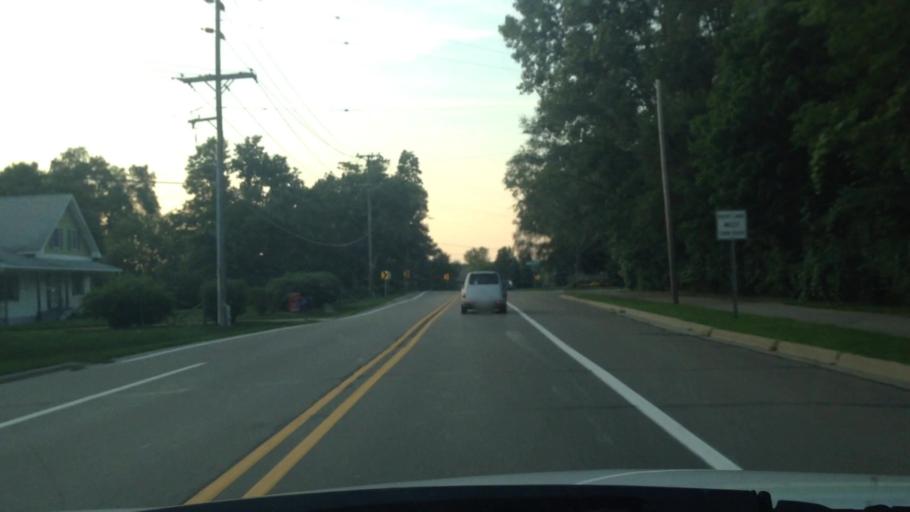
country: US
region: Michigan
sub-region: Oakland County
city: Lake Orion
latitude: 42.7415
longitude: -83.3083
